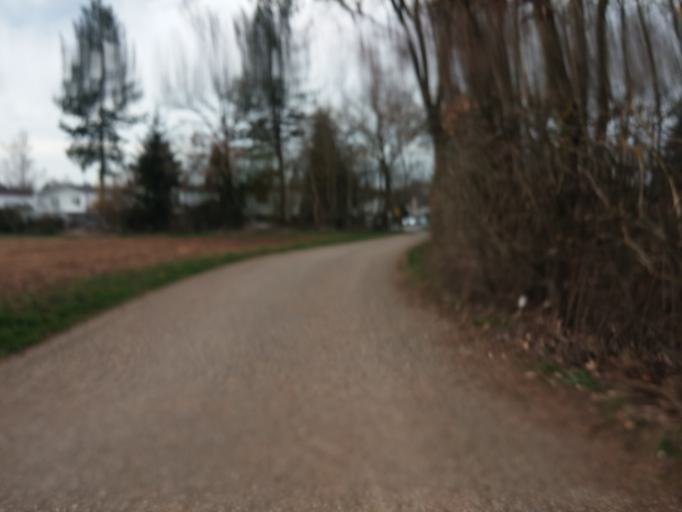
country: DE
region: Bavaria
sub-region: Upper Bavaria
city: Haar
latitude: 48.1012
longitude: 11.7358
